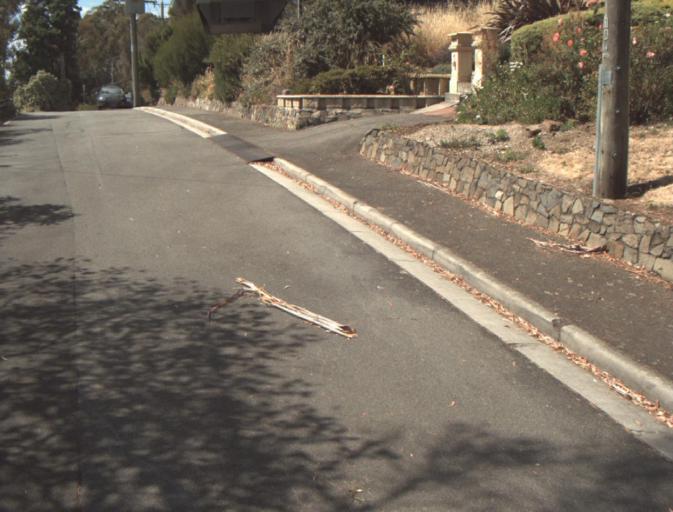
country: AU
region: Tasmania
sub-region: Launceston
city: West Launceston
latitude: -41.4494
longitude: 147.1235
